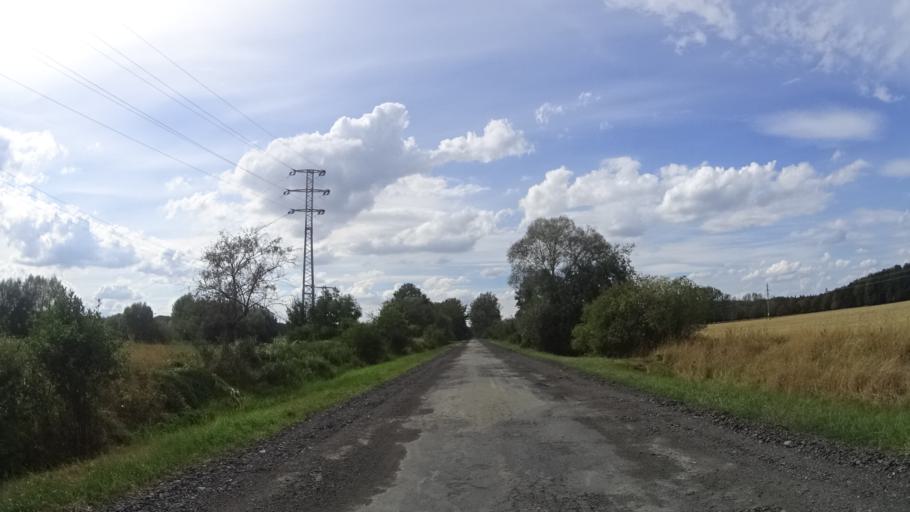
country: CZ
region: Olomoucky
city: Cervenka
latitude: 49.7147
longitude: 17.0530
